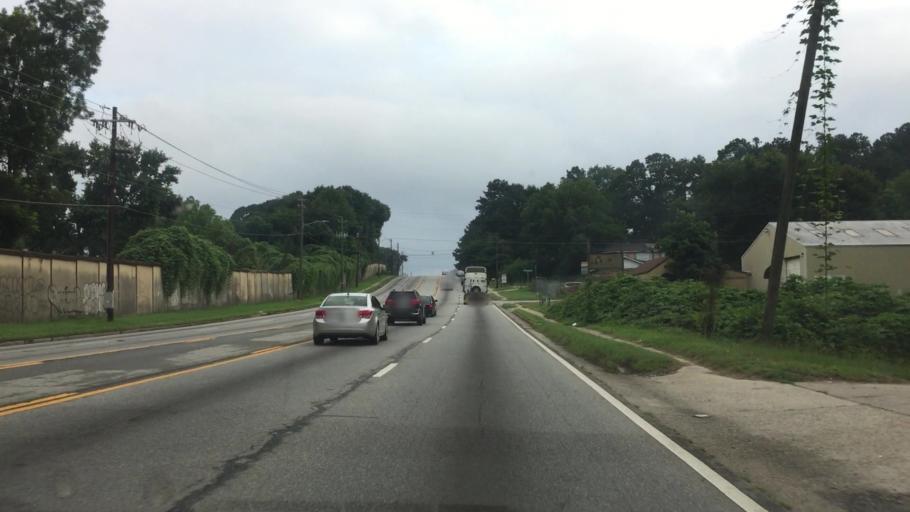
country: US
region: Georgia
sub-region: DeKalb County
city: Gresham Park
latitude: 33.6978
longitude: -84.3495
